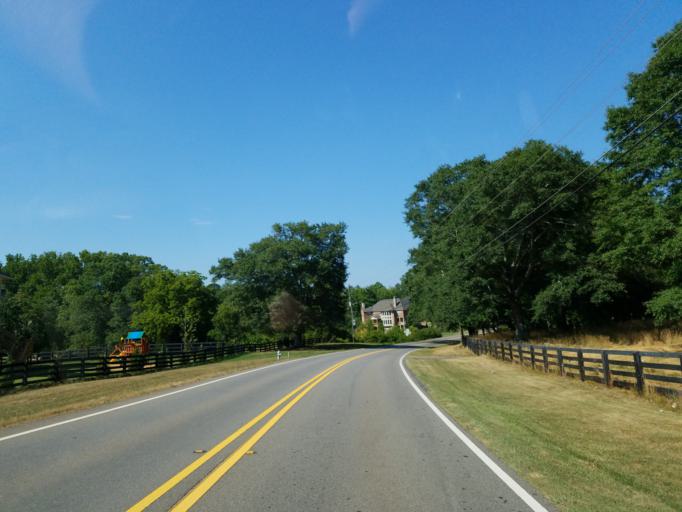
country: US
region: Georgia
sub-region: Fulton County
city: Milton
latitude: 34.1805
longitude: -84.3245
